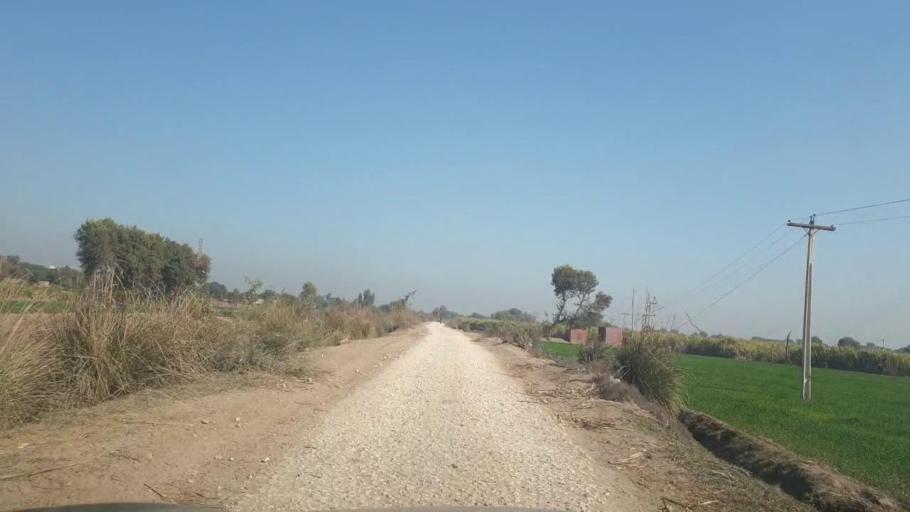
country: PK
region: Sindh
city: Mirpur Mathelo
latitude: 28.1255
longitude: 69.4954
